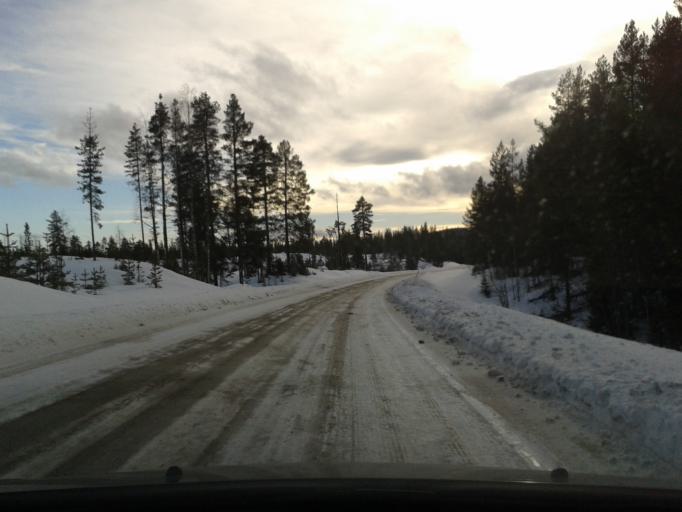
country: SE
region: Vaesterbotten
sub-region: Asele Kommun
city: Asele
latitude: 64.2659
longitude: 17.2746
